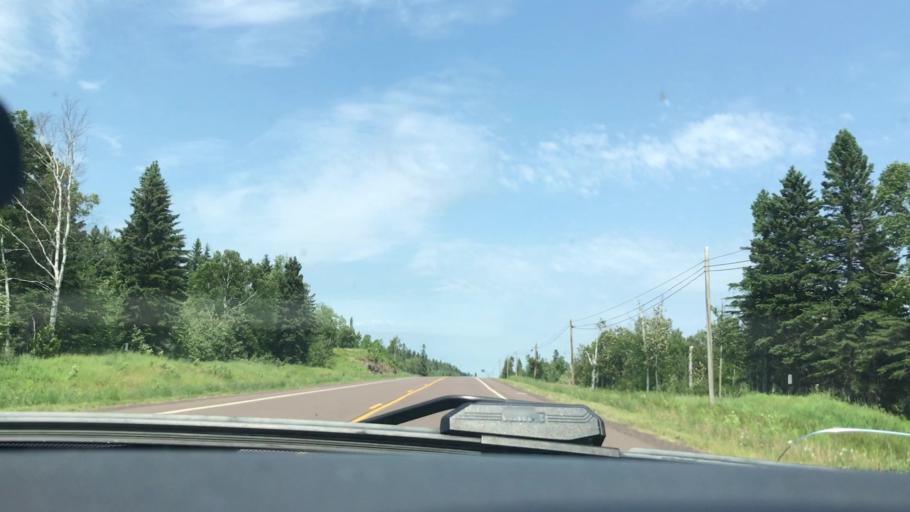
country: US
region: Minnesota
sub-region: Lake County
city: Silver Bay
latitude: 47.4295
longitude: -91.0878
